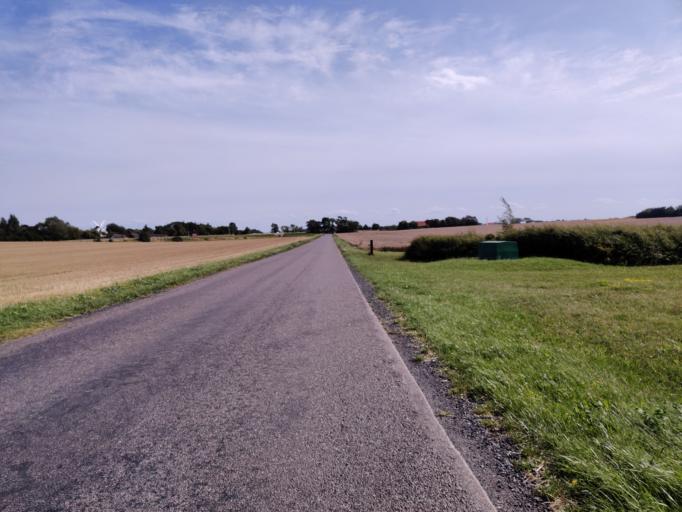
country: DK
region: Zealand
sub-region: Guldborgsund Kommune
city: Nykobing Falster
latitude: 54.6039
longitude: 11.9307
